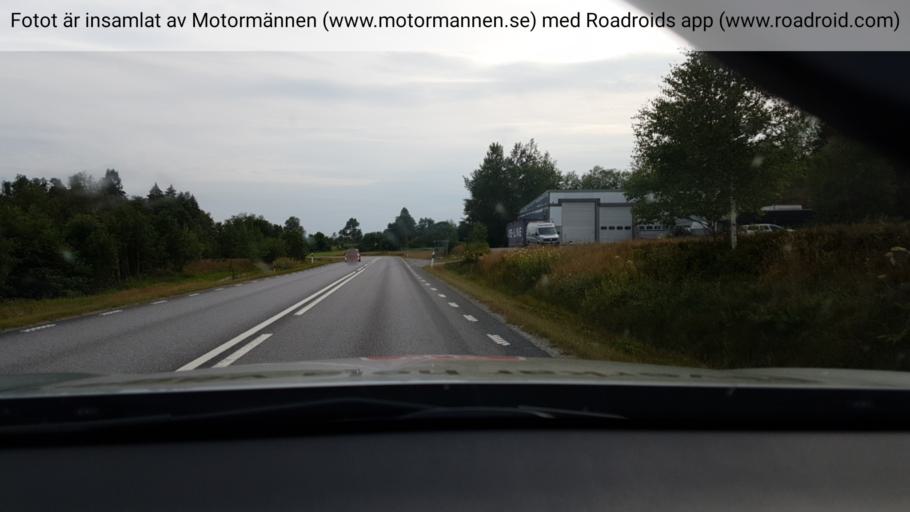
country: SE
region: Vaestra Goetaland
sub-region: Uddevalla Kommun
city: Uddevalla
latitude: 58.4114
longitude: 12.0124
